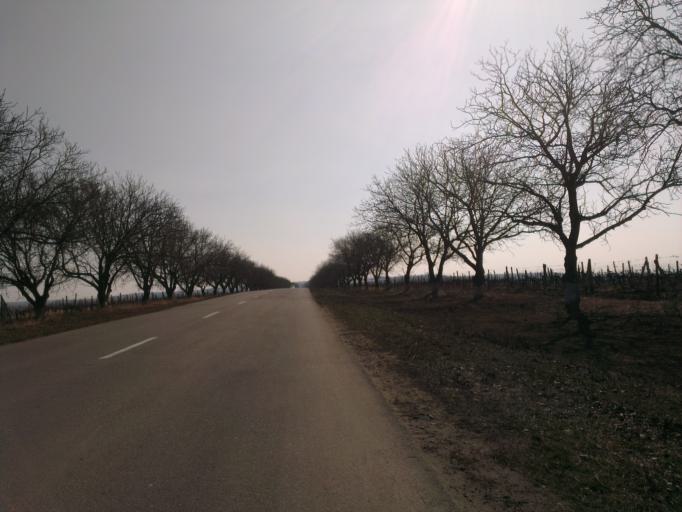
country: MD
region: Chisinau
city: Cricova
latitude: 47.1271
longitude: 28.8549
